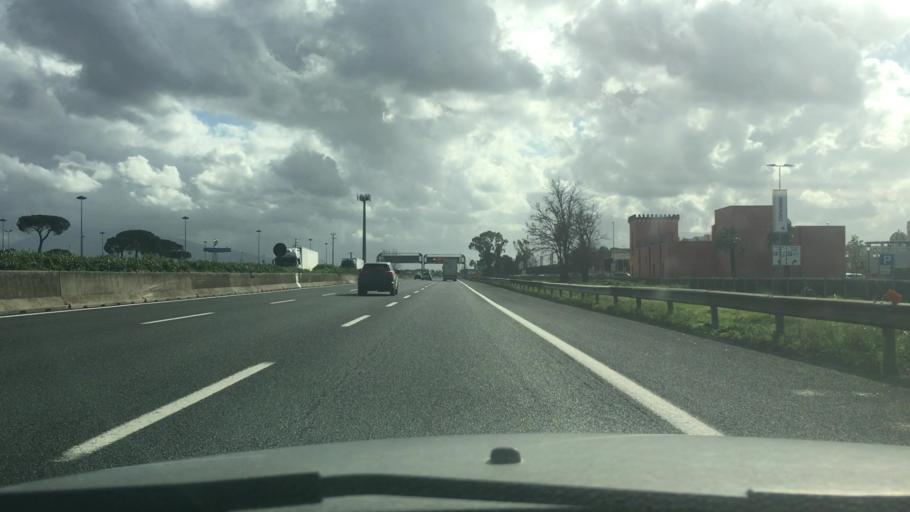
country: IT
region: Campania
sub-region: Provincia di Caserta
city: Marcianise
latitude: 41.0095
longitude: 14.3230
